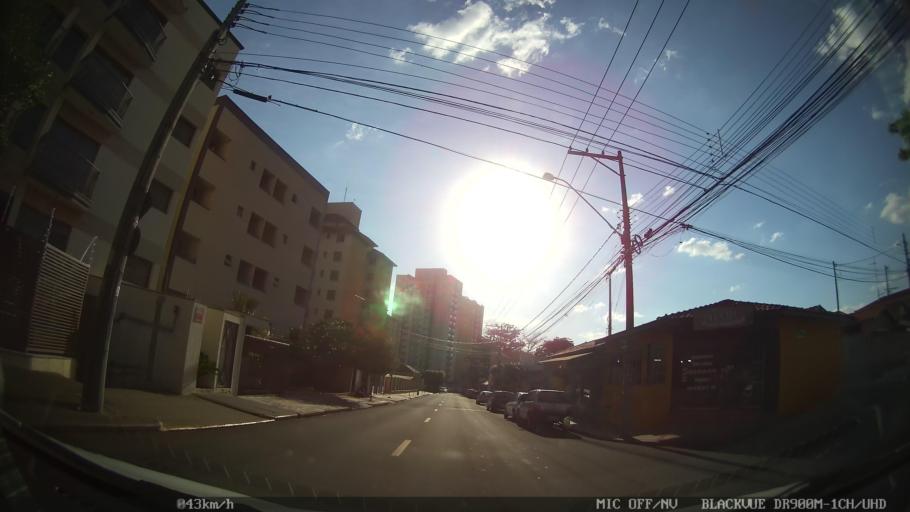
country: BR
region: Sao Paulo
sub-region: Ribeirao Preto
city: Ribeirao Preto
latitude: -21.1957
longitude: -47.7805
